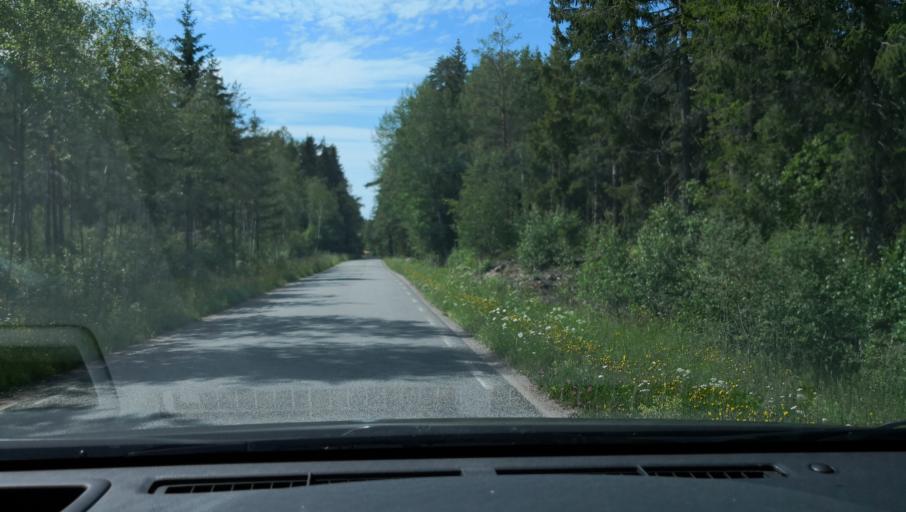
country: SE
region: Stockholm
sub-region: Sigtuna Kommun
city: Sigtuna
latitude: 59.6895
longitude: 17.6581
